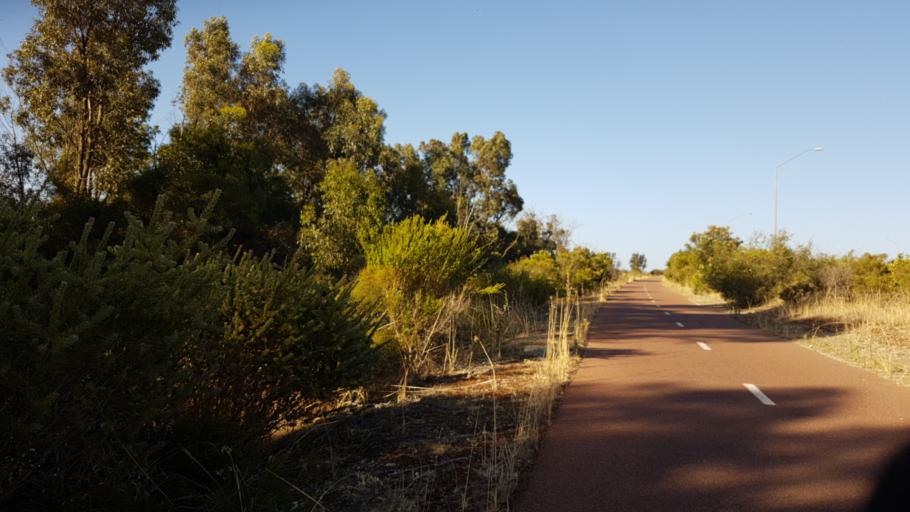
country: AU
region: Western Australia
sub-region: Kwinana
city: Wellard
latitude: -32.2757
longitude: 115.8410
